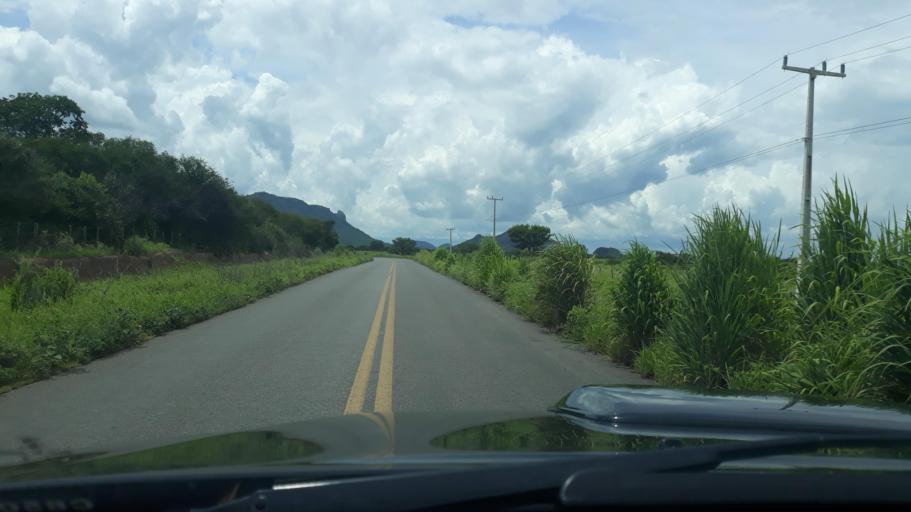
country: BR
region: Bahia
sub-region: Guanambi
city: Guanambi
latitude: -14.1641
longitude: -42.8158
